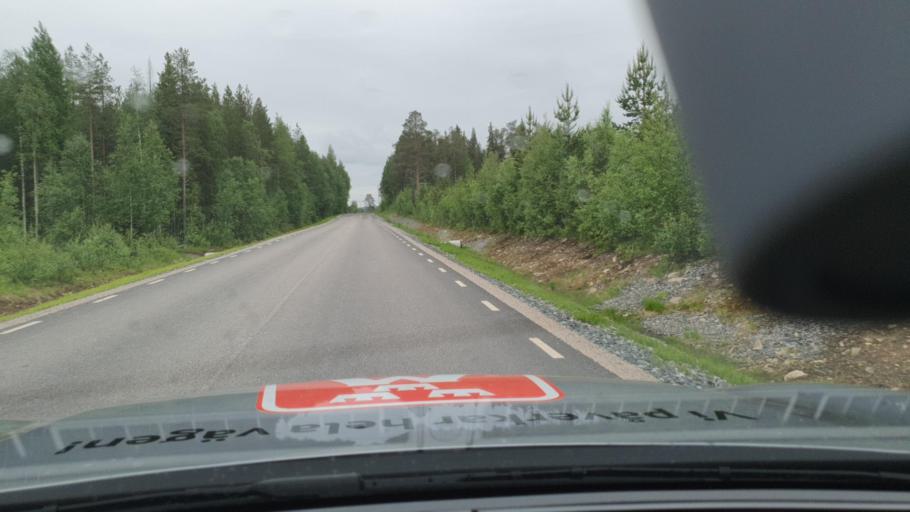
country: SE
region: Norrbotten
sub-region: Overtornea Kommun
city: OEvertornea
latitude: 66.5735
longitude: 23.3317
